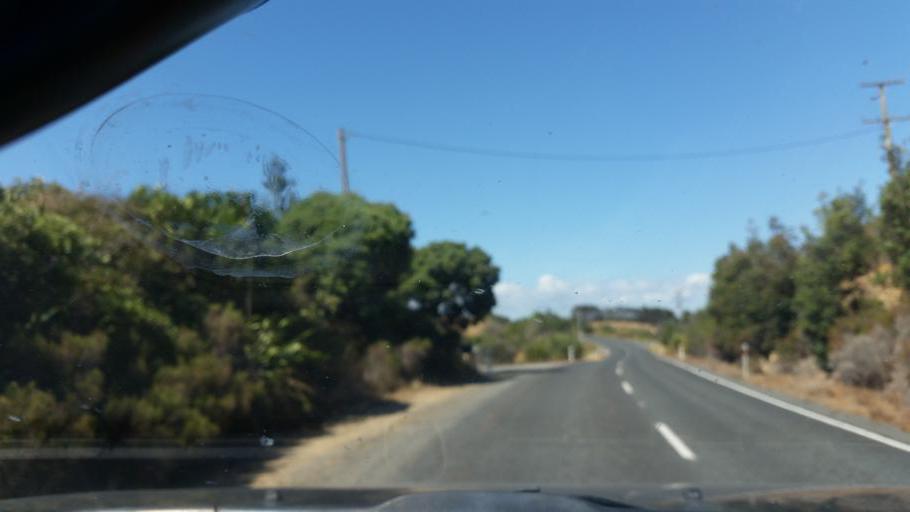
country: NZ
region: Northland
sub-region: Kaipara District
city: Dargaville
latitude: -35.9500
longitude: 173.7558
